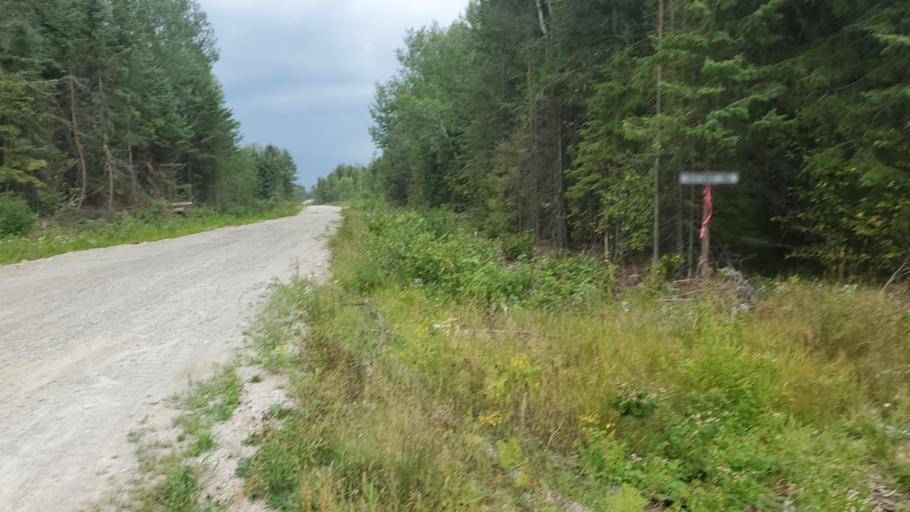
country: CA
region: Ontario
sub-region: Rainy River District
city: Atikokan
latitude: 49.5973
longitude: -91.3831
